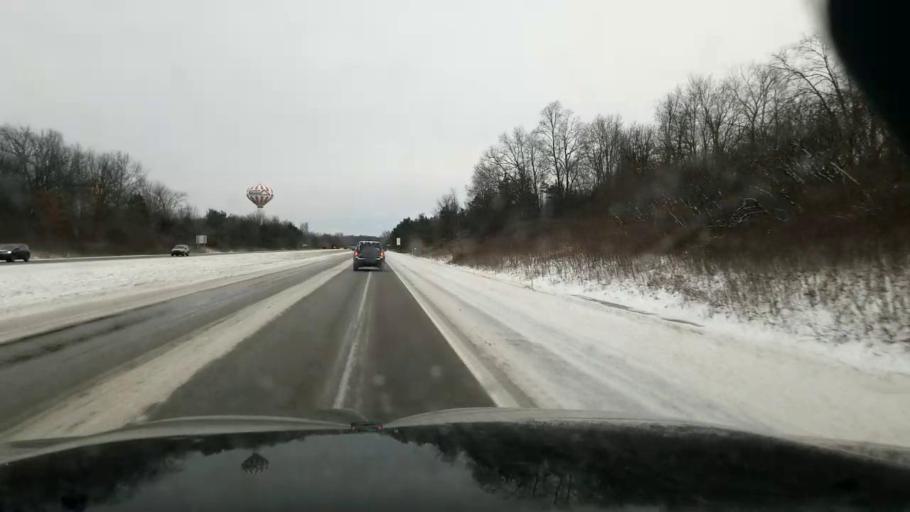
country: US
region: Michigan
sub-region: Jackson County
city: Jackson
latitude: 42.2449
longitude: -84.4759
